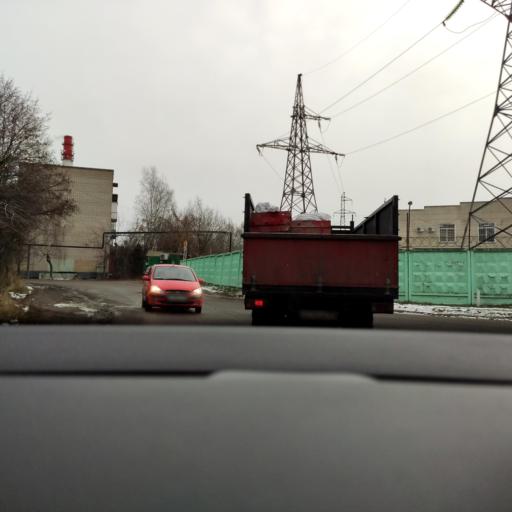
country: RU
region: Moskovskaya
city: Golitsyno
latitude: 55.6281
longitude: 37.0079
